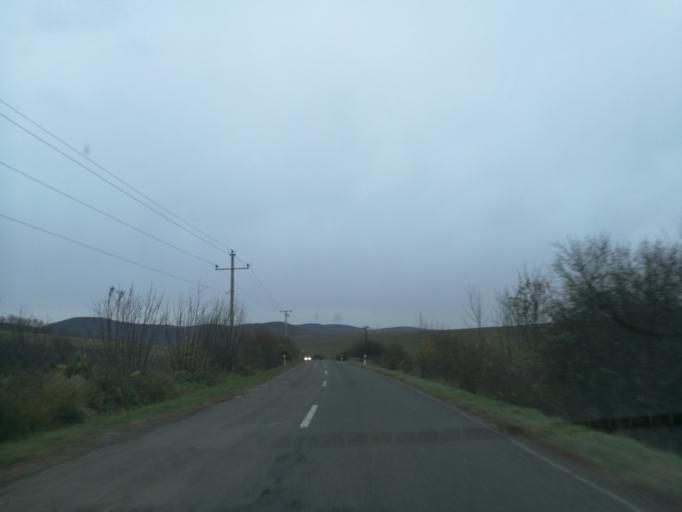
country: HU
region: Nograd
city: Rimoc
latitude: 48.0133
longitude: 19.5987
